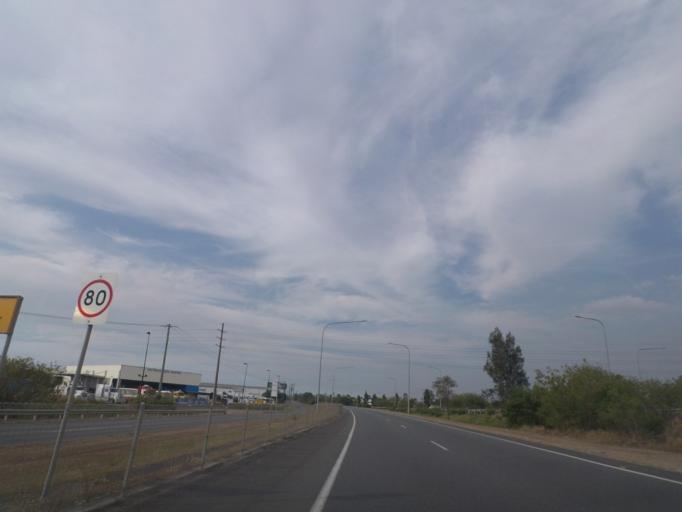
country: AU
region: Queensland
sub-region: Brisbane
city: Rocklea
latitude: -27.5542
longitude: 153.0087
